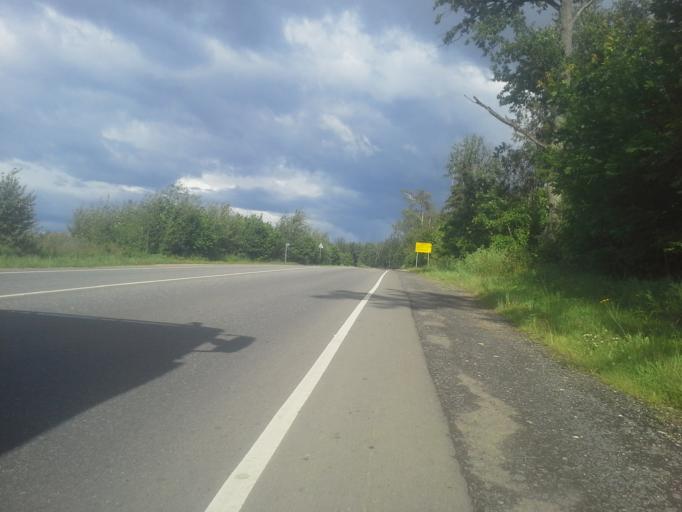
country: RU
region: Moskovskaya
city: Zvenigorod
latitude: 55.7029
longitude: 36.8347
